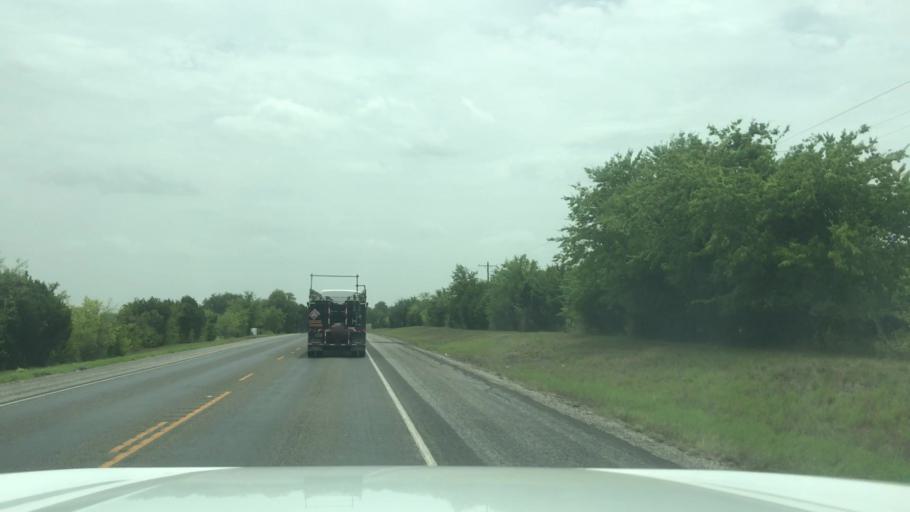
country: US
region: Texas
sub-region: Bosque County
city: Meridian
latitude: 31.8689
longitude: -97.6354
